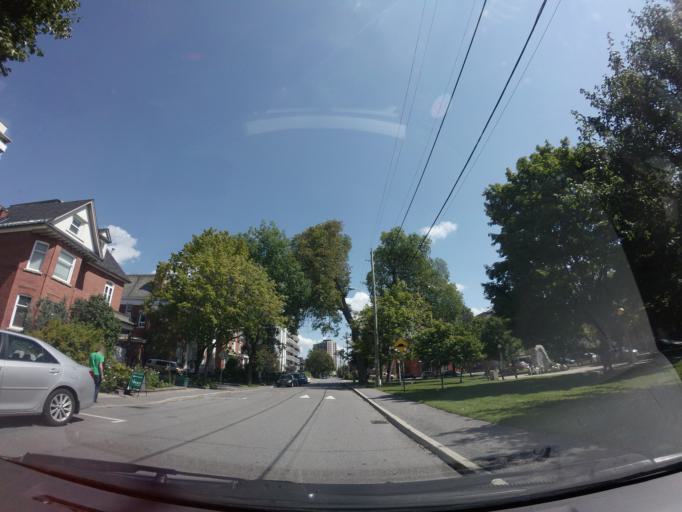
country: CA
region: Ontario
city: Ottawa
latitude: 45.4170
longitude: -75.6880
